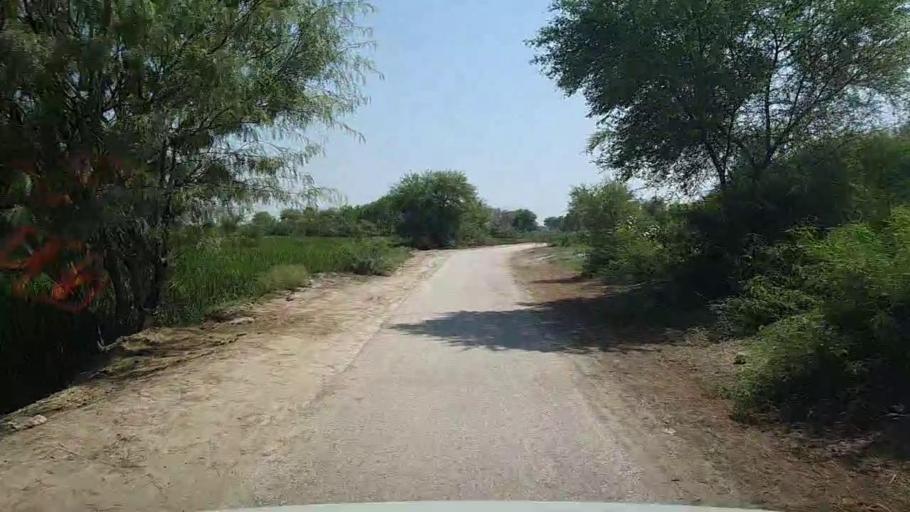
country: PK
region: Sindh
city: Kandhkot
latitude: 28.2844
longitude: 69.3543
